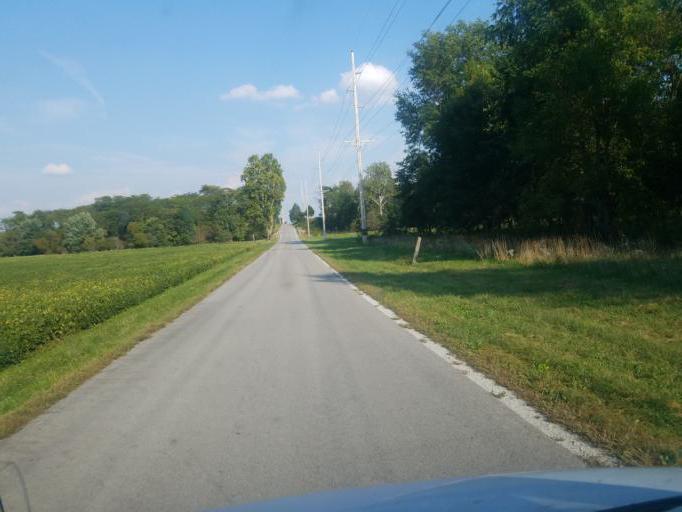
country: US
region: Ohio
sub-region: Wyandot County
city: Carey
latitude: 40.9237
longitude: -83.3151
